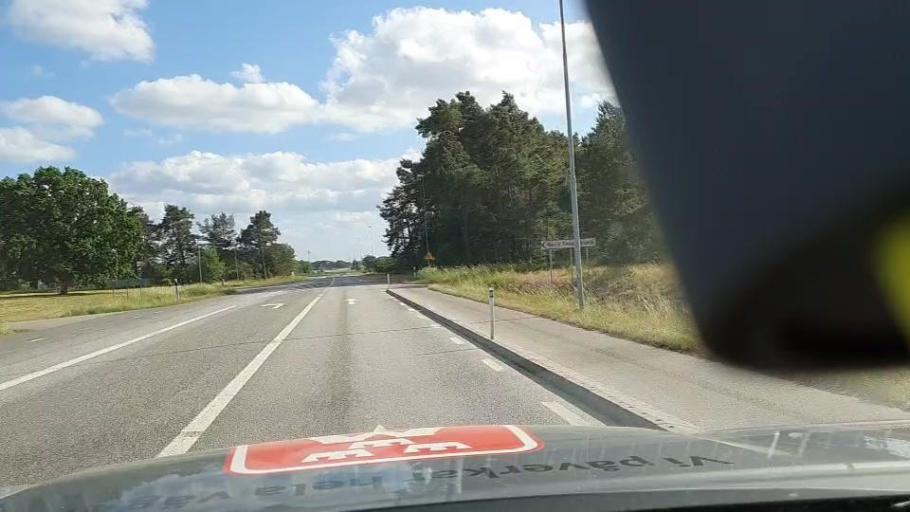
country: SE
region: Blekinge
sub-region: Solvesborgs Kommun
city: Soelvesborg
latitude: 56.0871
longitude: 14.6481
